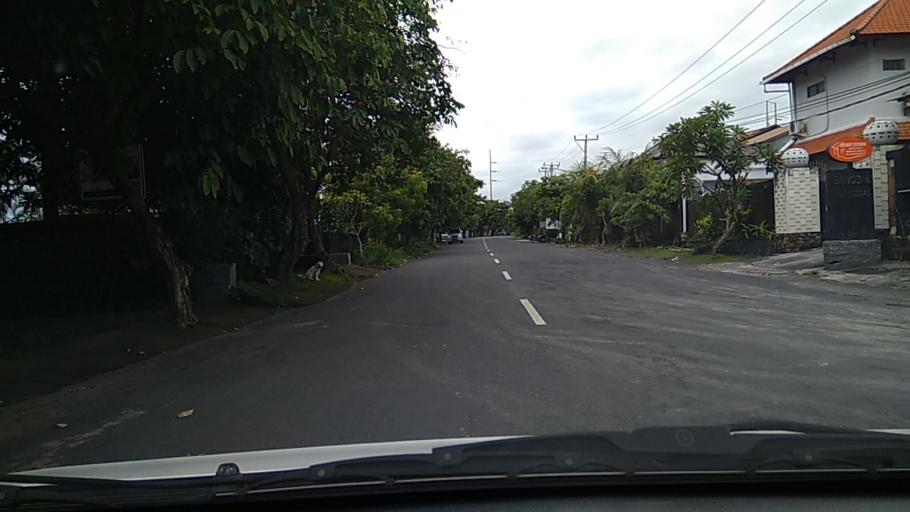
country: ID
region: Bali
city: Banjar Kertajiwa
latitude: -8.6573
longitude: 115.2600
